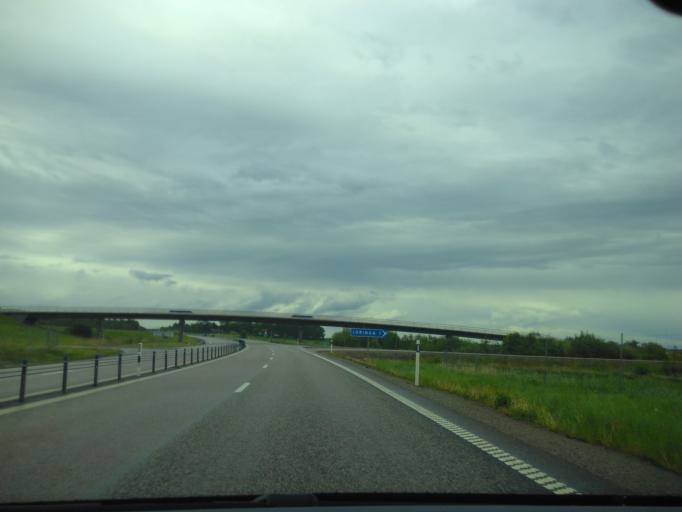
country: SE
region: Vaestra Goetaland
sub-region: Skovde Kommun
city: Skultorp
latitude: 58.3219
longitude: 13.8335
